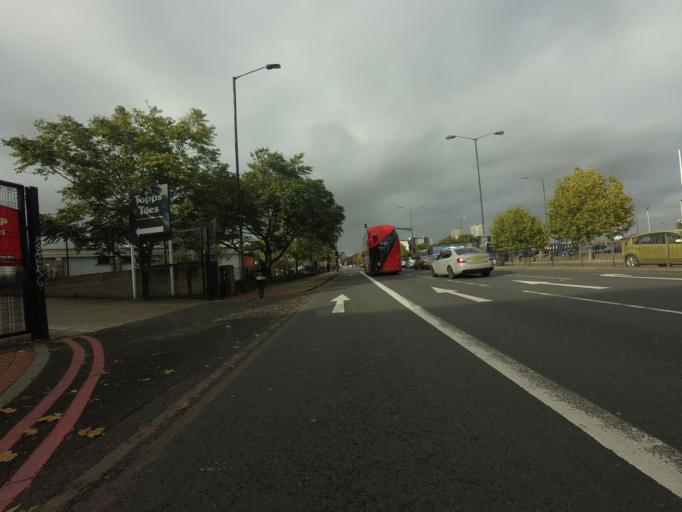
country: GB
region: England
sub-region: Greater London
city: Camberwell
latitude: 51.4836
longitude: -0.0656
